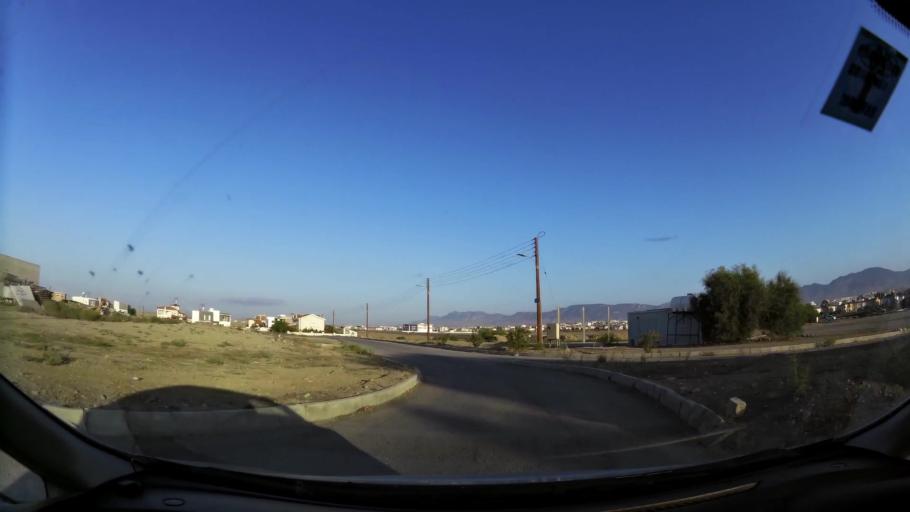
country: CY
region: Lefkosia
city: Nicosia
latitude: 35.1951
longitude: 33.3168
